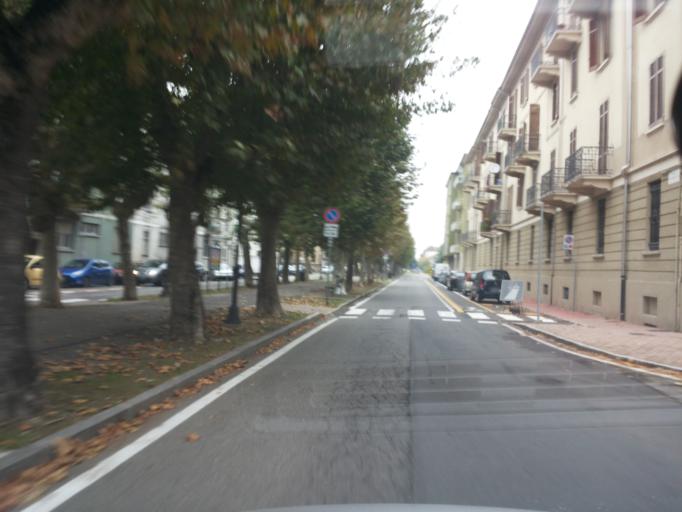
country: IT
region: Piedmont
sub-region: Provincia di Vercelli
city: Vercelli
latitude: 45.3285
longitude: 8.4338
